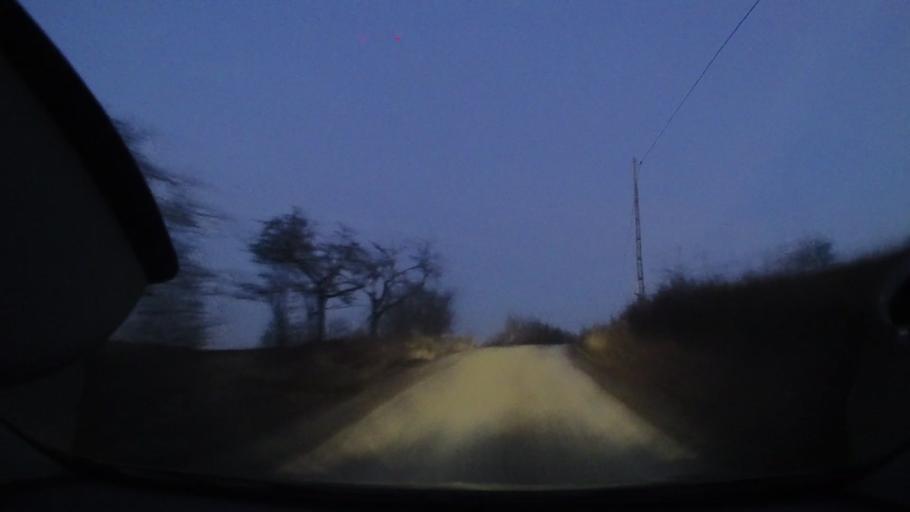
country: RO
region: Bihor
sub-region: Comuna Varciorog
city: Varciorog
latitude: 46.9922
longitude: 22.3225
